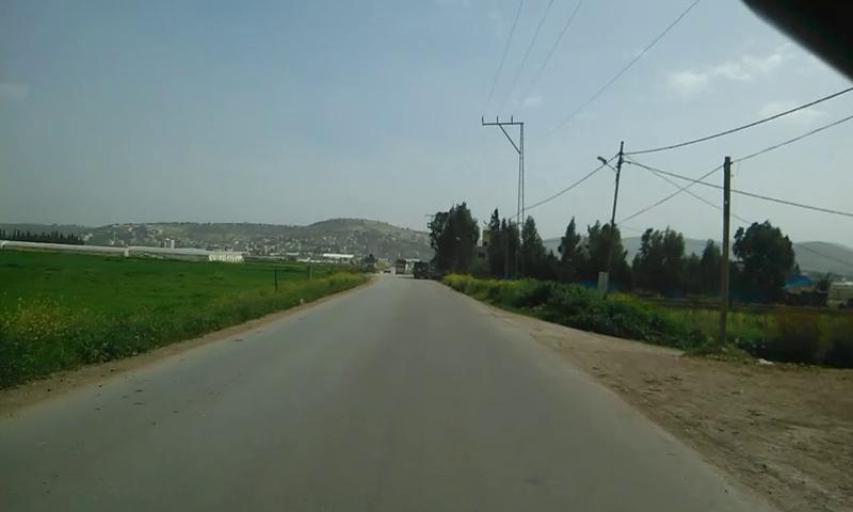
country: PS
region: West Bank
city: Ash Shuhada'
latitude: 32.4394
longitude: 35.2639
